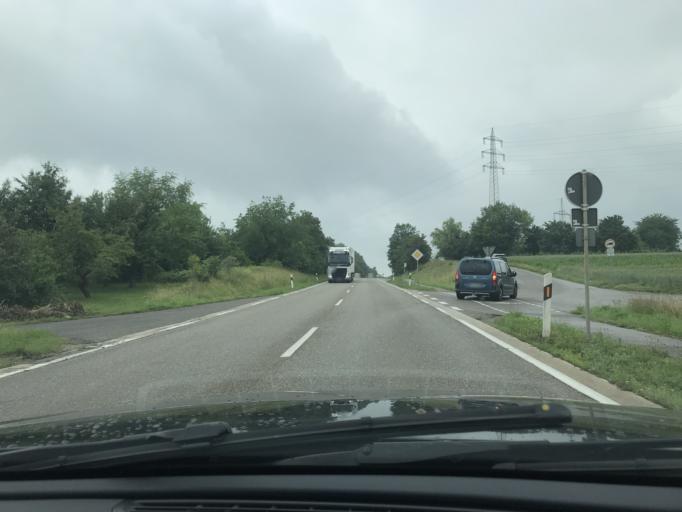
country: DE
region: Baden-Wuerttemberg
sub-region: Regierungsbezirk Stuttgart
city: Waiblingen
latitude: 48.8436
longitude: 9.3049
